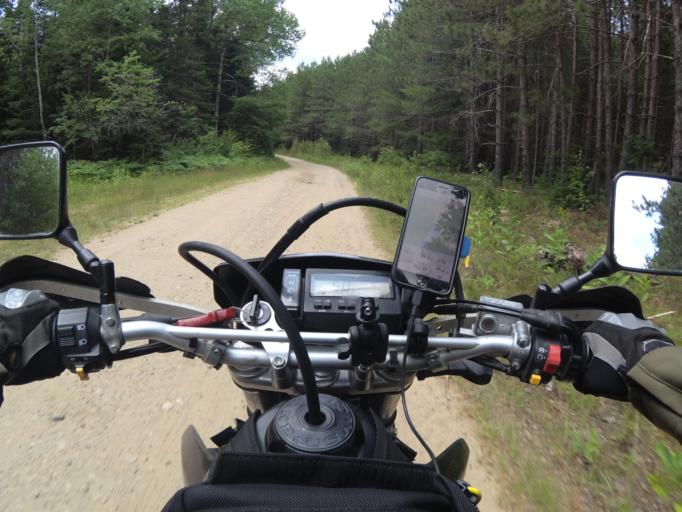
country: CA
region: Ontario
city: Bancroft
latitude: 45.0199
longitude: -77.2648
